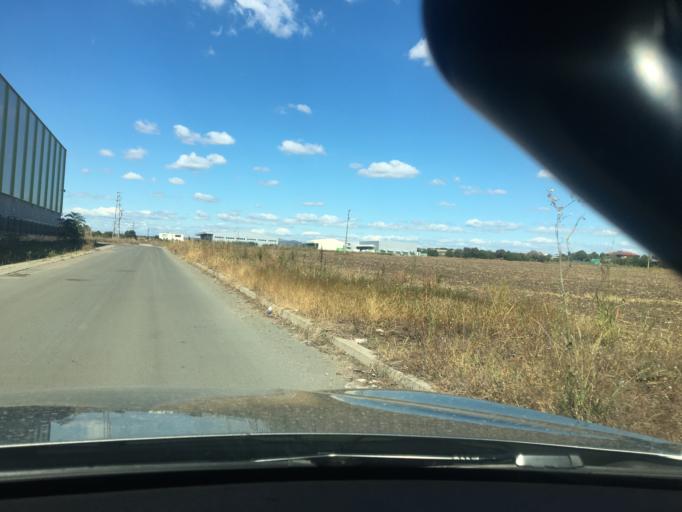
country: BG
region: Burgas
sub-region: Obshtina Burgas
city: Burgas
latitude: 42.5346
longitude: 27.4525
